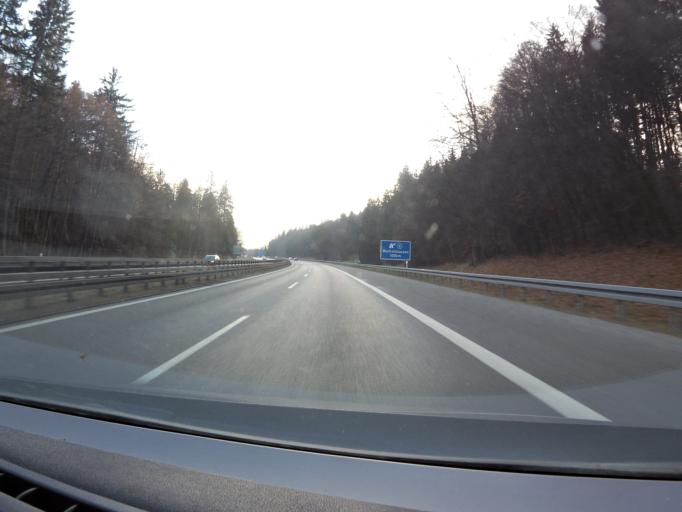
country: DE
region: Bavaria
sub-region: Upper Bavaria
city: Wolfratshausen
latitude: 47.9163
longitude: 11.3952
